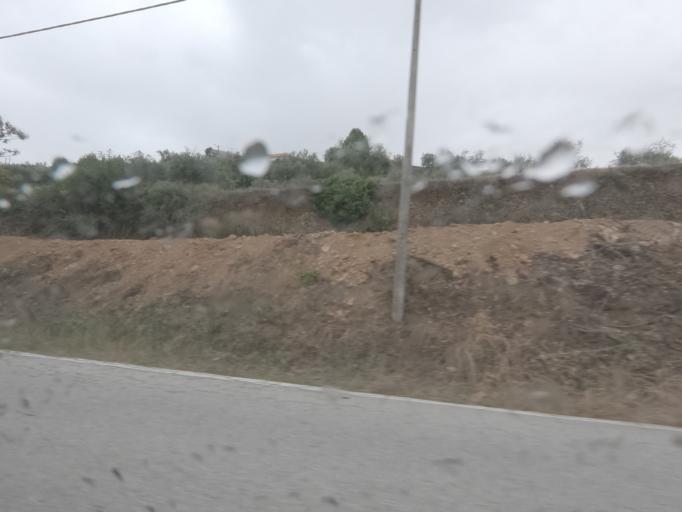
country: PT
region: Viseu
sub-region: Armamar
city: Armamar
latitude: 41.1161
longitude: -7.7204
